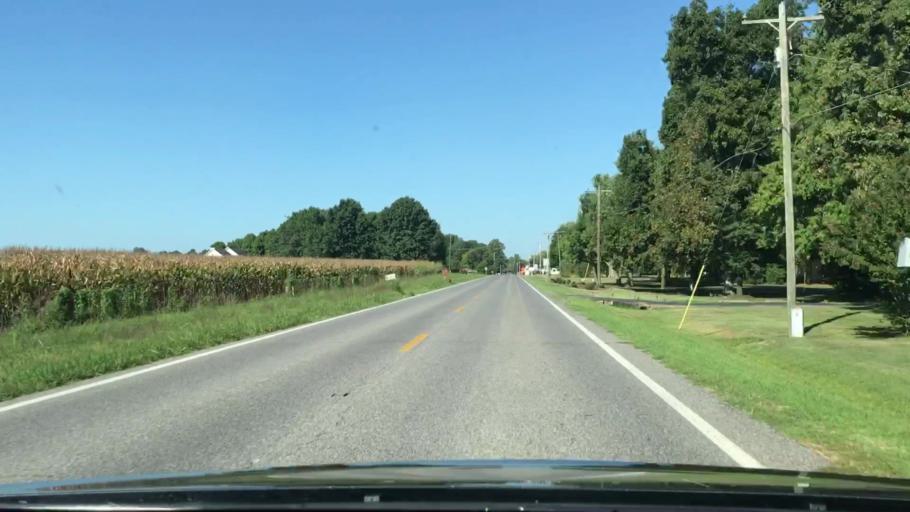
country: US
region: Kentucky
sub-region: Graves County
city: Mayfield
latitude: 36.7604
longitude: -88.5905
